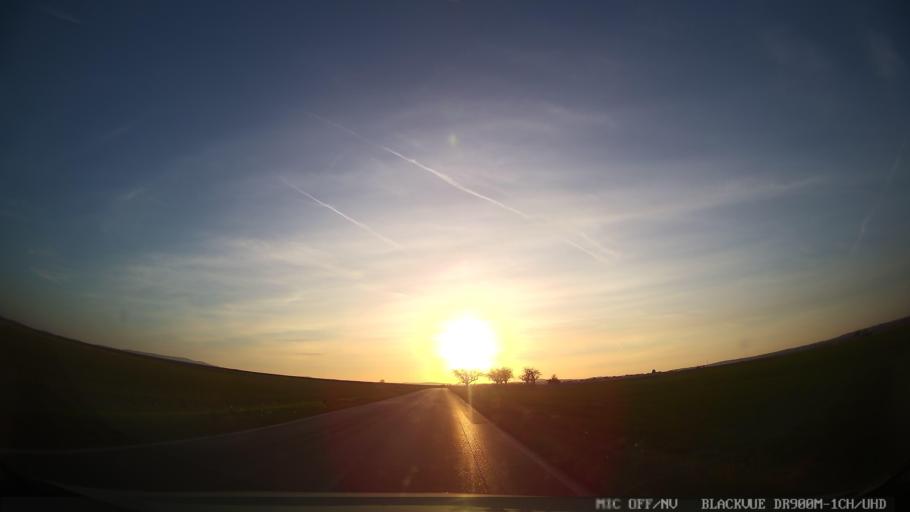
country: DE
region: Hesse
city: Dieburg
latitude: 49.8708
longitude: 8.8757
